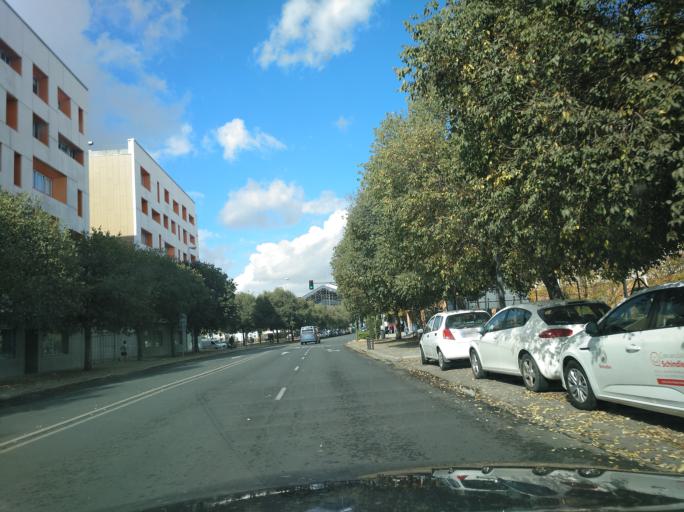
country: ES
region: Andalusia
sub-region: Provincia de Sevilla
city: Sevilla
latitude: 37.3808
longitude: -5.9832
